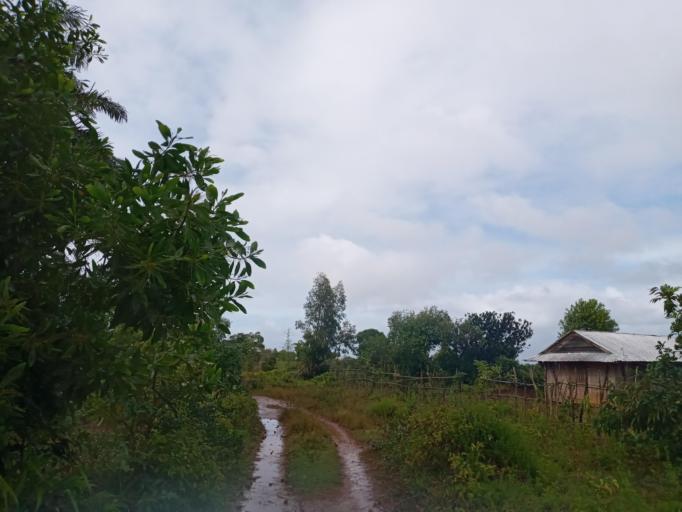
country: MG
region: Atsimo-Atsinanana
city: Vohipaho
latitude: -23.7918
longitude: 47.5464
